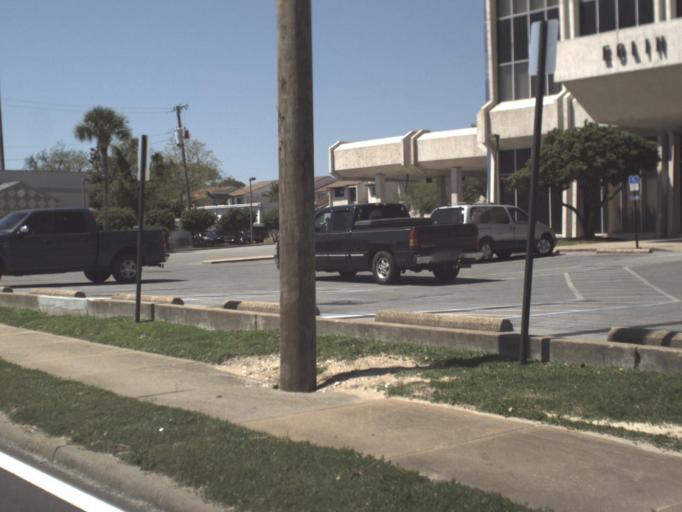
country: US
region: Florida
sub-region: Okaloosa County
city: Ocean City
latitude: 30.4414
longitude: -86.5936
